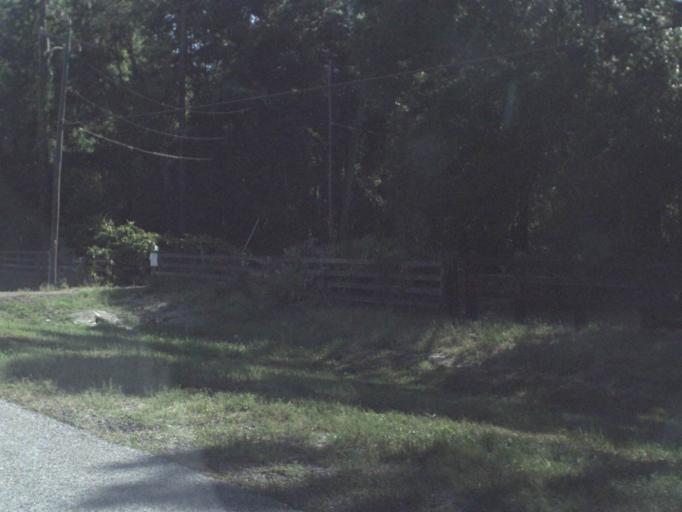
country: US
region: Florida
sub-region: Alachua County
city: Hawthorne
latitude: 29.5499
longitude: -82.0986
